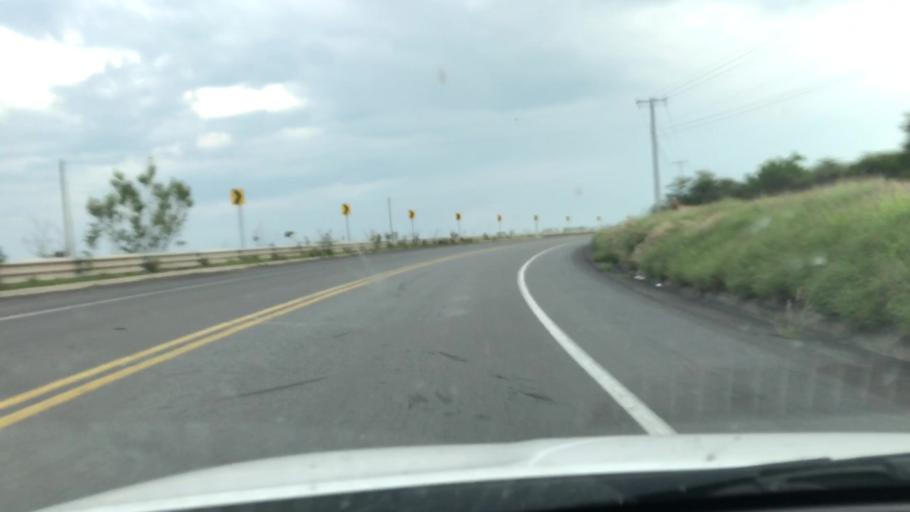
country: MX
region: Michoacan
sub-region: Yurecuaro
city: Yurecuaro
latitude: 20.3437
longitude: -102.1611
